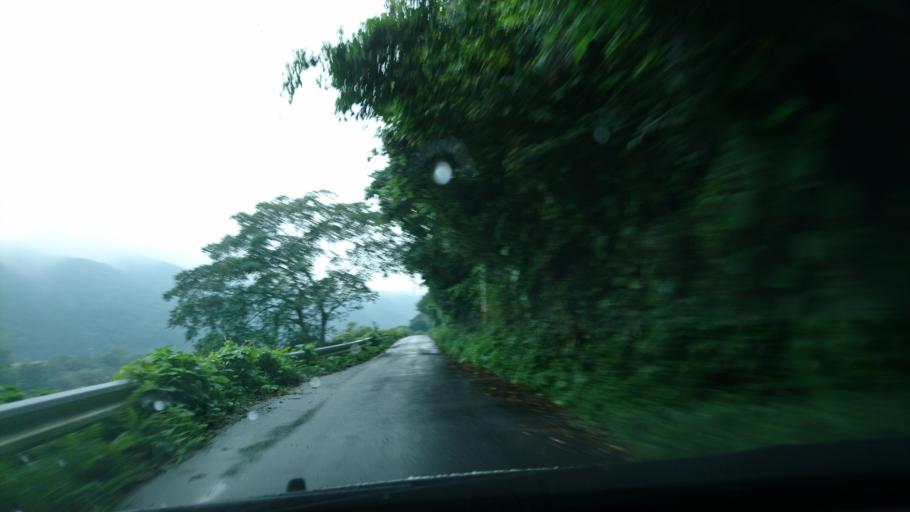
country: JP
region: Iwate
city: Ichinoseki
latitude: 38.8734
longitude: 141.2603
